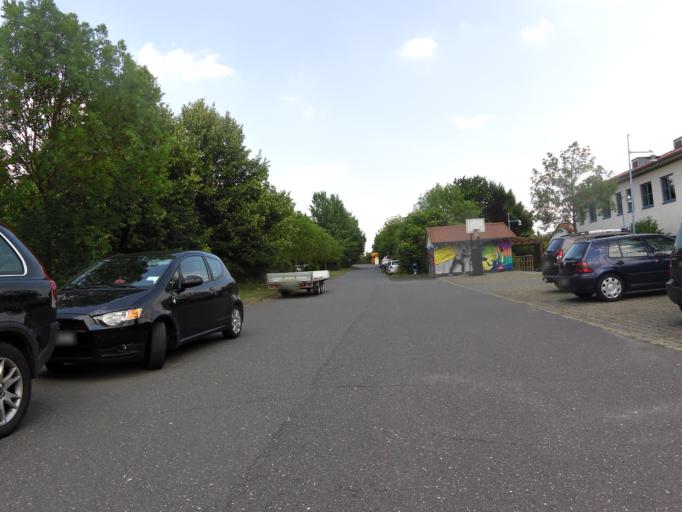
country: DE
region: Bavaria
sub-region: Regierungsbezirk Unterfranken
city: Randersacker
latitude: 49.7321
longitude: 9.9675
